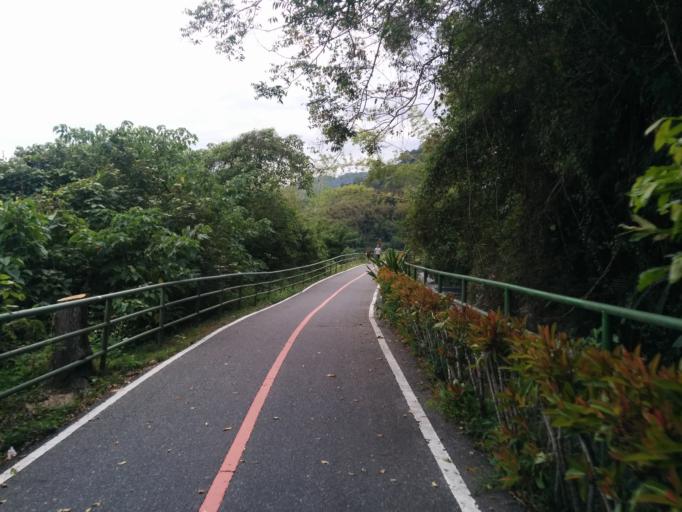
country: TW
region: Taiwan
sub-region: Taitung
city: Taitung
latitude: 23.0570
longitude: 121.1593
